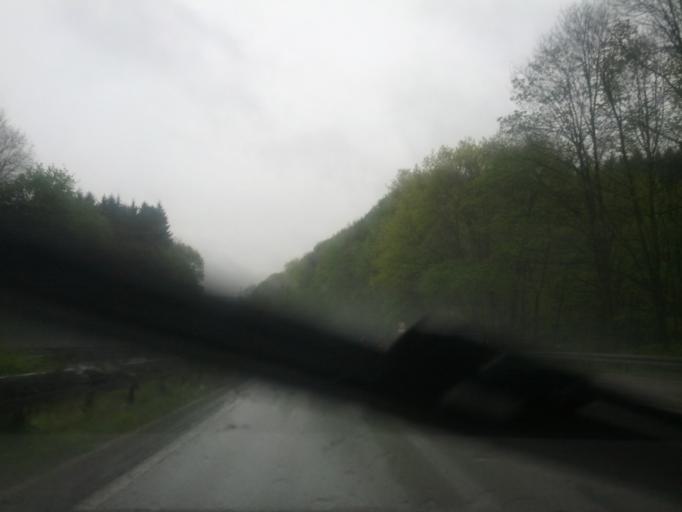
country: DE
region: North Rhine-Westphalia
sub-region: Regierungsbezirk Koln
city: Rosrath
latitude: 50.9514
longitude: 7.2005
